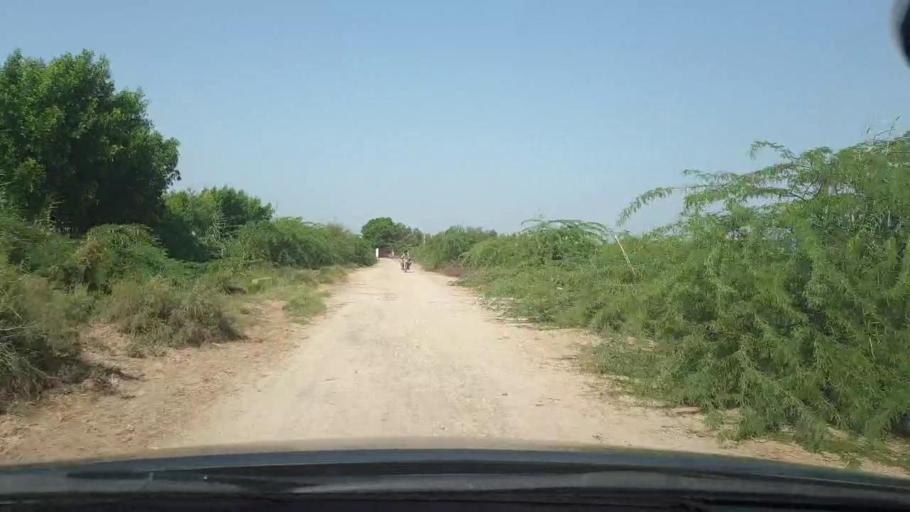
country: PK
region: Sindh
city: Tando Bago
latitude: 24.7197
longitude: 69.0971
